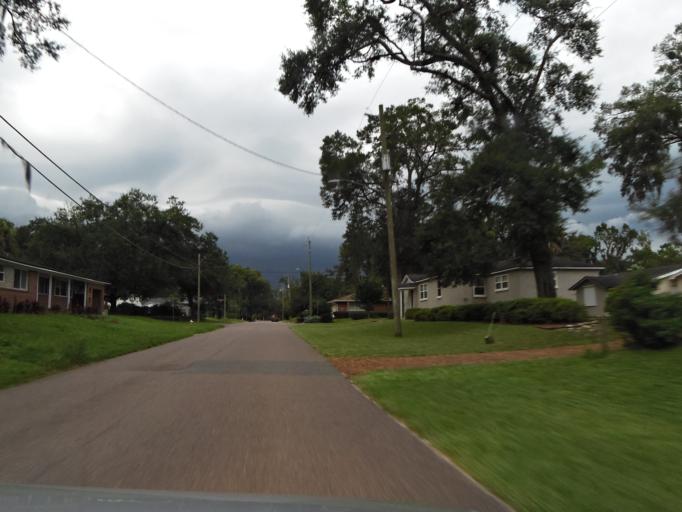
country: US
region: Florida
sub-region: Duval County
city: Jacksonville
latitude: 30.2958
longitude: -81.7113
